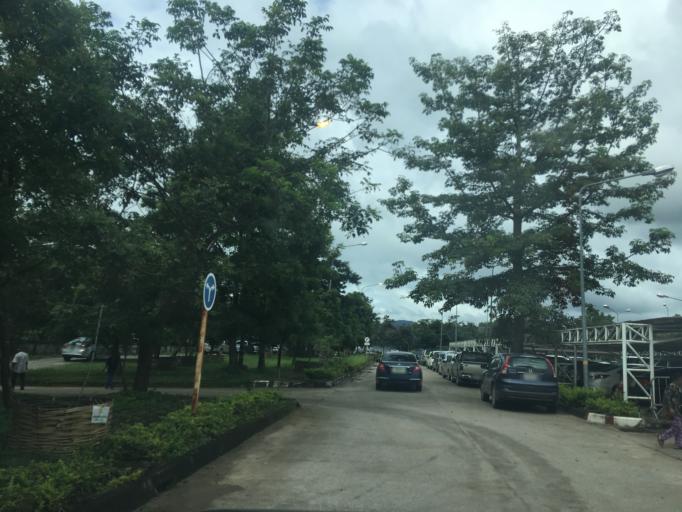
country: TH
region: Chiang Rai
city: Chiang Rai
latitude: 19.9199
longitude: 99.8147
